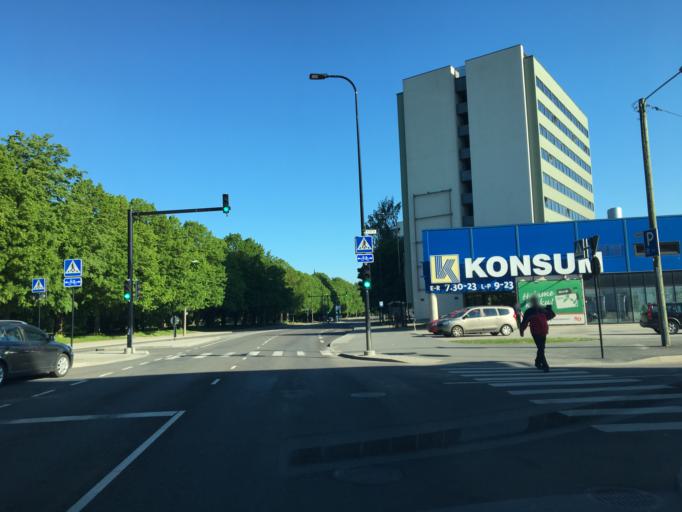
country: EE
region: Tartu
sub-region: Tartu linn
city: Tartu
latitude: 58.3820
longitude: 26.7286
